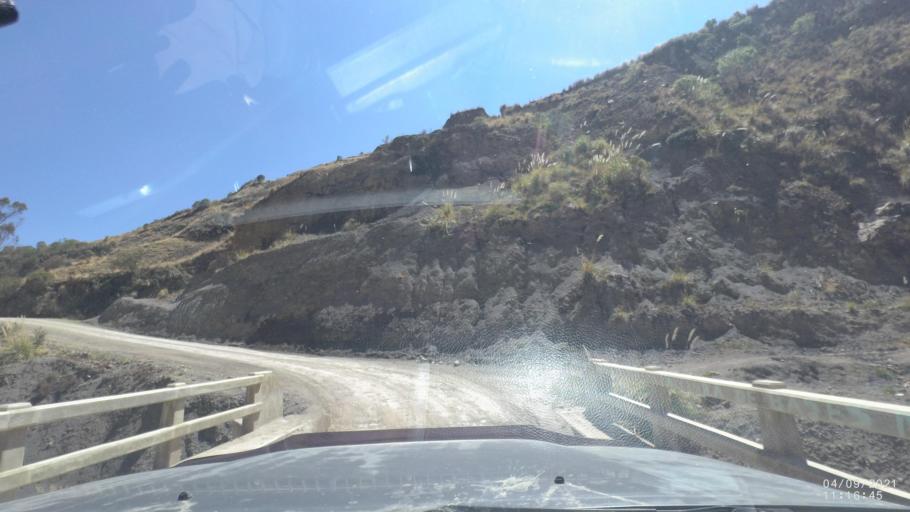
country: BO
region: Cochabamba
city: Sipe Sipe
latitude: -17.2712
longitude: -66.4847
